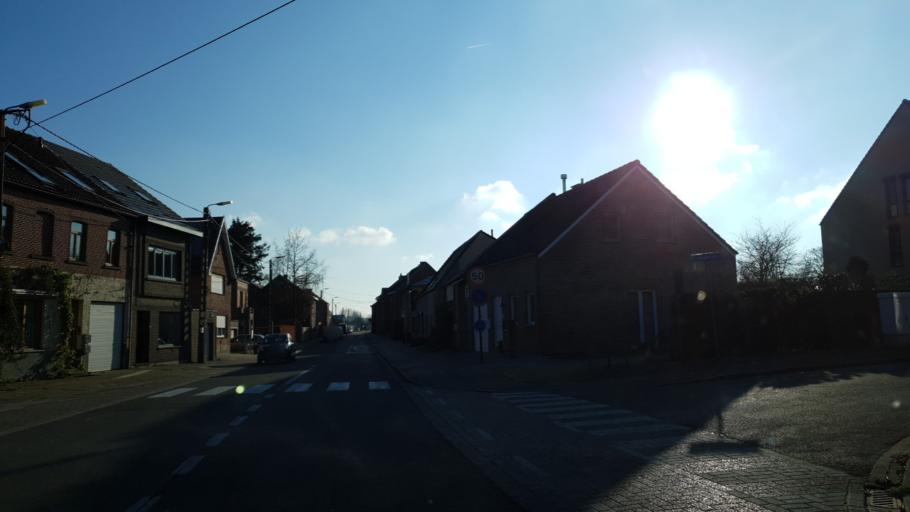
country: BE
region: Flanders
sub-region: Provincie Vlaams-Brabant
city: Herent
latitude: 50.9176
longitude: 4.6978
